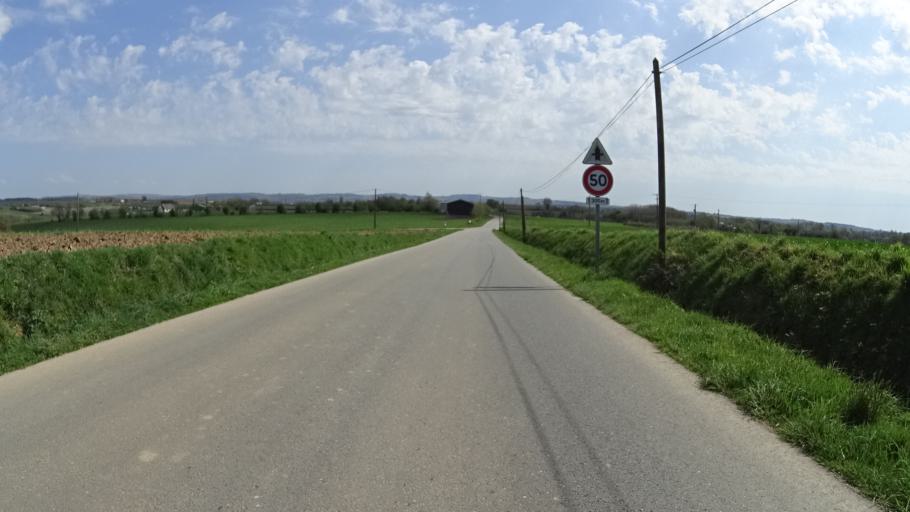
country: FR
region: Brittany
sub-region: Departement du Finistere
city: Sizun
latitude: 48.4305
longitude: -4.1155
